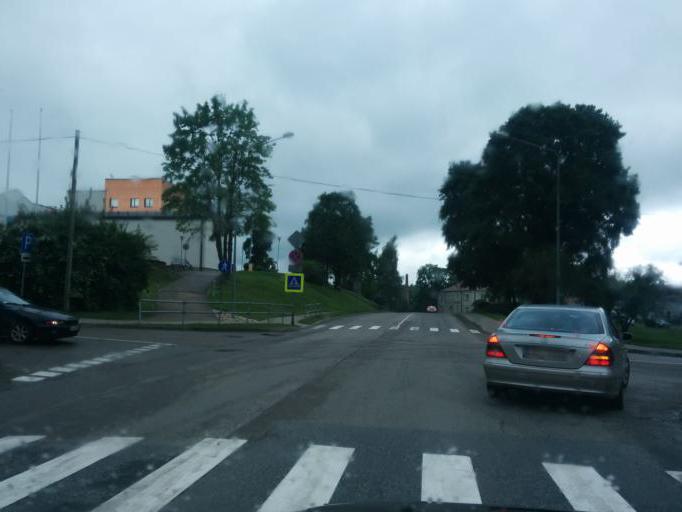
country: LV
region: Smiltene
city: Smiltene
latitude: 57.4224
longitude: 25.9049
